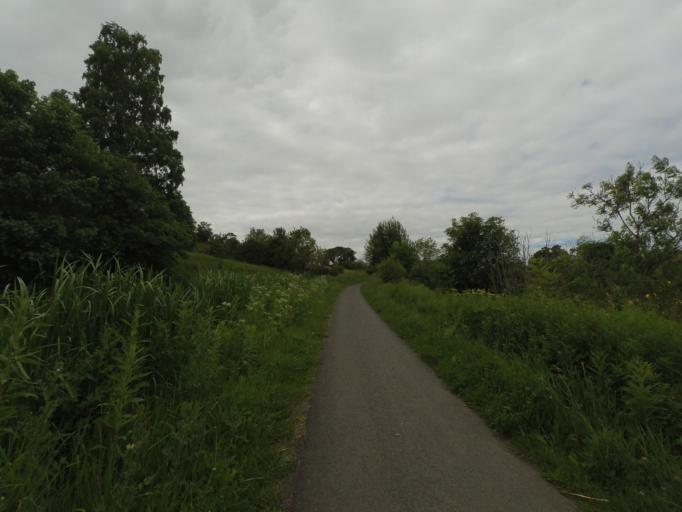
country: GB
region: Scotland
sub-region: West Lothian
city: Linlithgow
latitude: 55.9669
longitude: -3.6338
